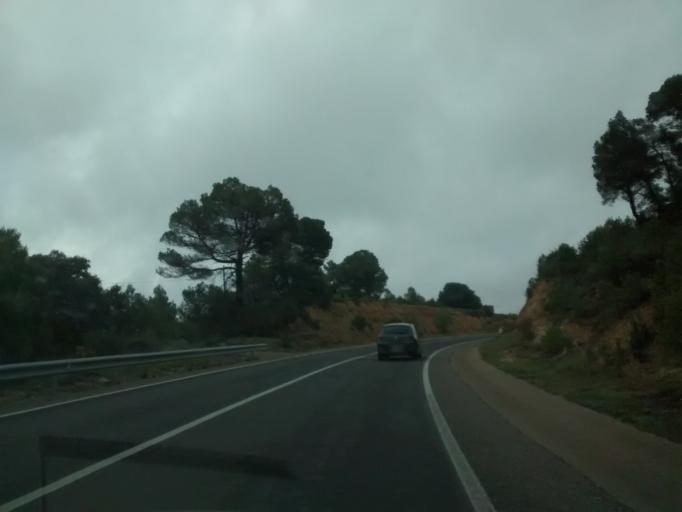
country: ES
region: Catalonia
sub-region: Provincia de Tarragona
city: Bot
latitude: 41.0579
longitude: 0.3594
